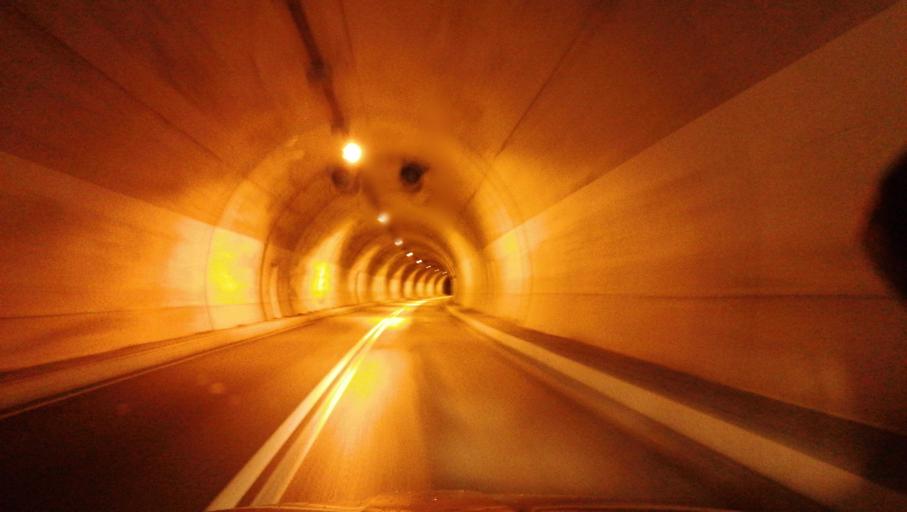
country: BA
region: Republika Srpska
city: Gacko
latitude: 43.2421
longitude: 18.6145
